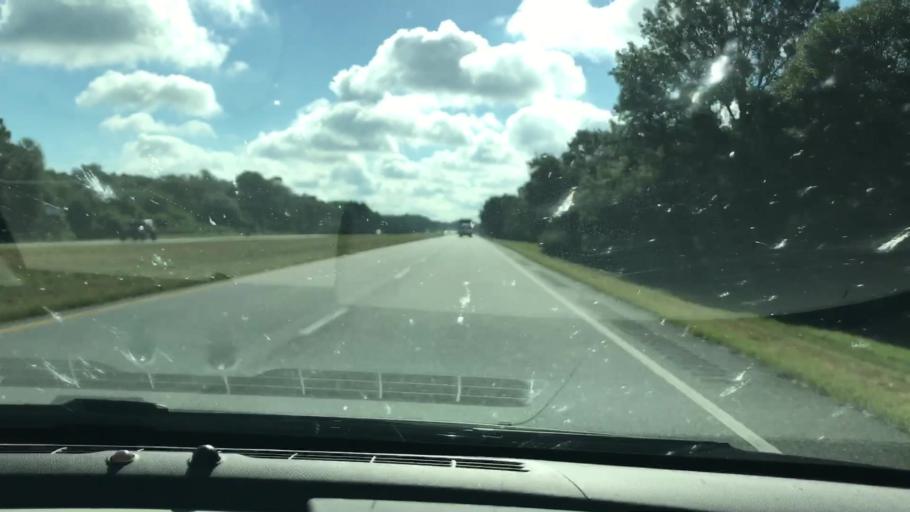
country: US
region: Georgia
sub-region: Worth County
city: Sylvester
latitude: 31.5537
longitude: -83.9847
